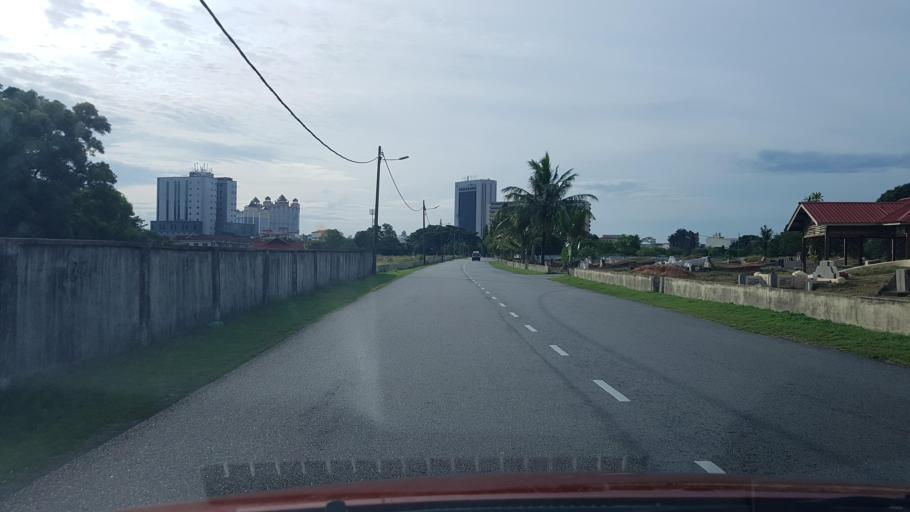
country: MY
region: Terengganu
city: Kuala Terengganu
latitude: 5.3236
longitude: 103.1450
